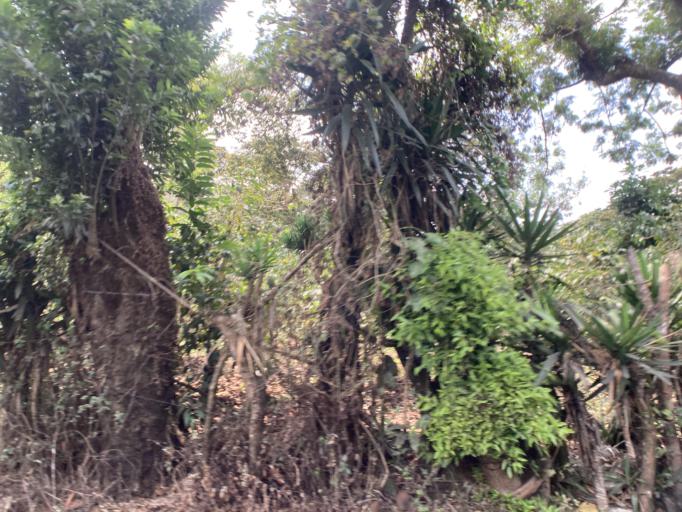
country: GT
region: Guatemala
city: Villa Canales
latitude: 14.4158
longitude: -90.5308
